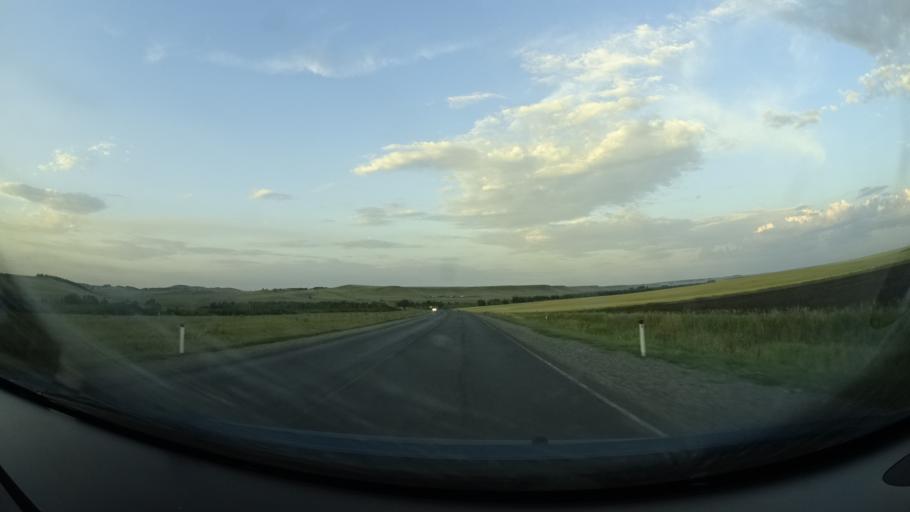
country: RU
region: Orenburg
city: Severnoye
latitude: 54.1302
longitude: 52.5824
